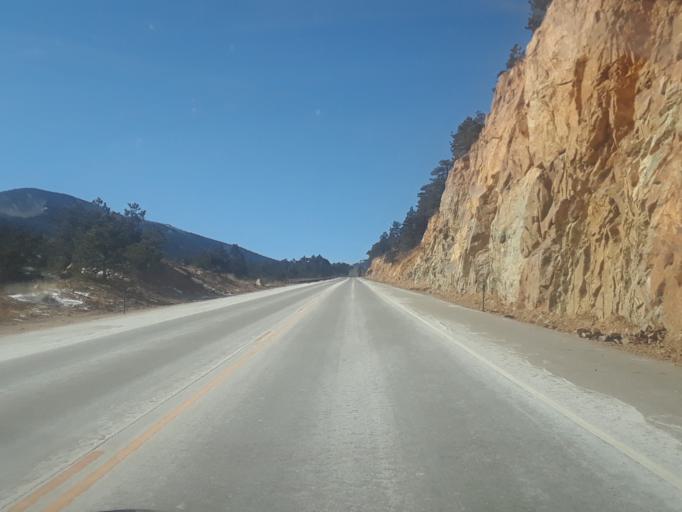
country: US
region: Colorado
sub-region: Larimer County
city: Estes Park
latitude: 40.1934
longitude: -105.5158
